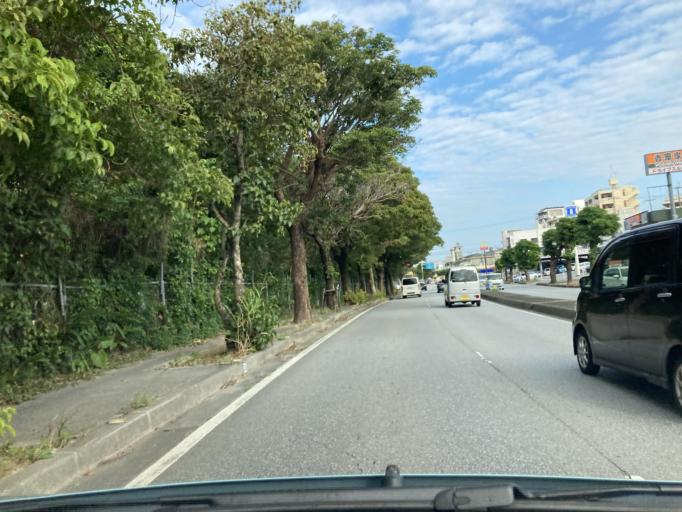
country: JP
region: Okinawa
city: Okinawa
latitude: 26.3361
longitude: 127.7912
